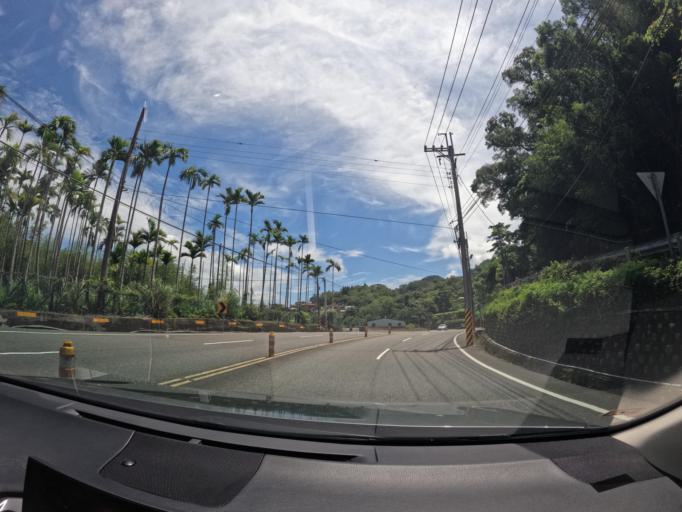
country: TW
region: Taiwan
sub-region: Miaoli
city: Miaoli
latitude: 24.4846
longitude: 120.8983
